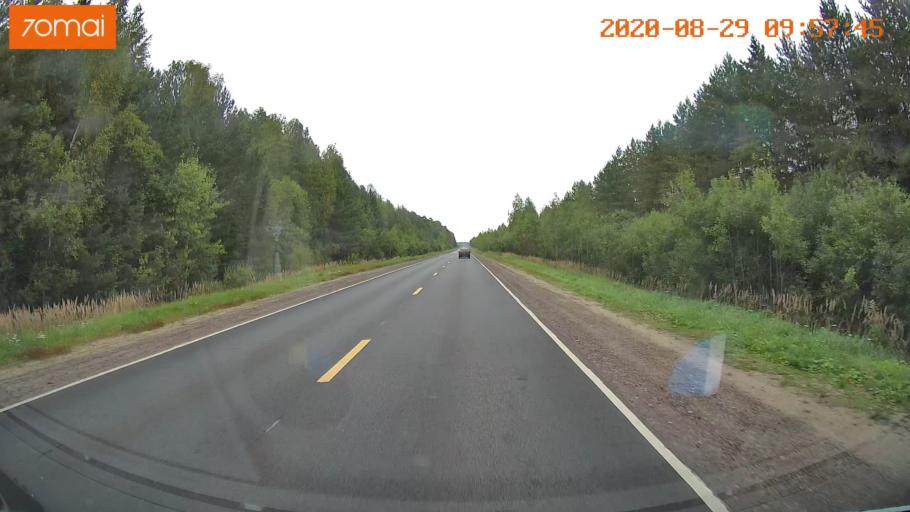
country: RU
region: Ivanovo
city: Zarechnyy
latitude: 57.4155
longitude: 42.3221
